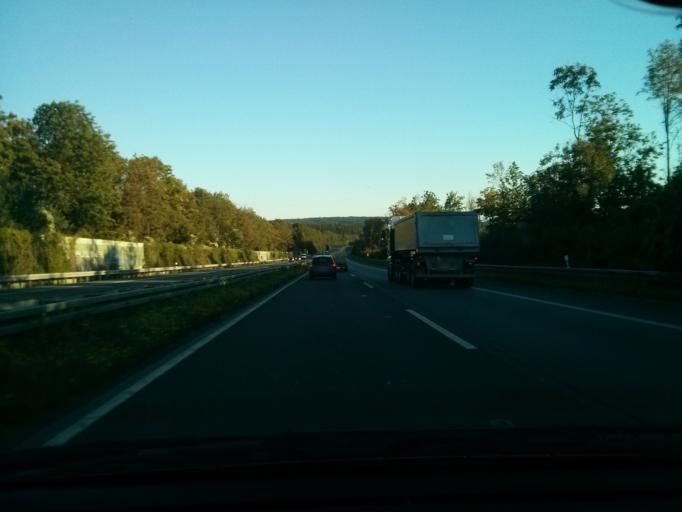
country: DE
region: North Rhine-Westphalia
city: Wickede
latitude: 51.5055
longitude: 7.9137
